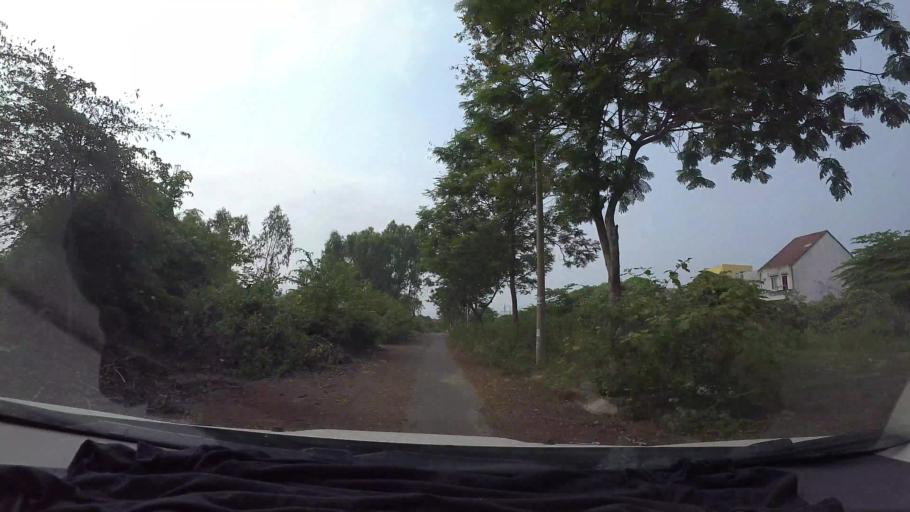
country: VN
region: Da Nang
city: Lien Chieu
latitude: 16.0568
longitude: 108.1599
